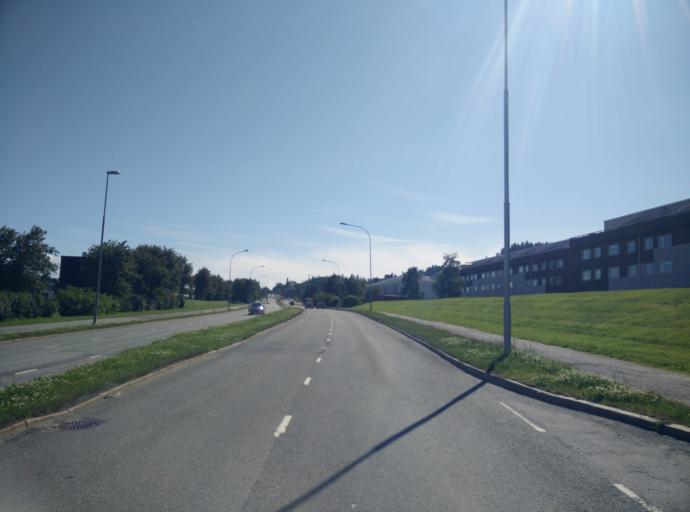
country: NO
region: Sor-Trondelag
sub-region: Trondheim
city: Trondheim
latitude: 63.4112
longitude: 10.3611
